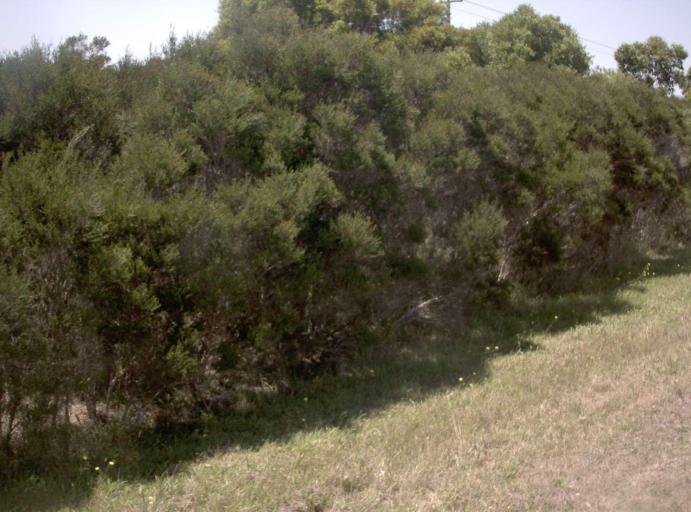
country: AU
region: Victoria
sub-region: Bass Coast
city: North Wonthaggi
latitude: -38.6425
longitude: 145.8500
